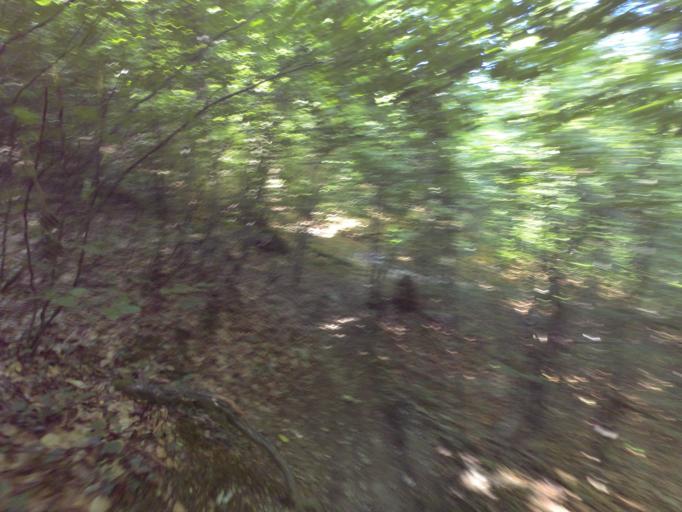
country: AT
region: Salzburg
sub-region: Politischer Bezirk Salzburg-Umgebung
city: Elsbethen
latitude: 47.7659
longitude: 13.1011
